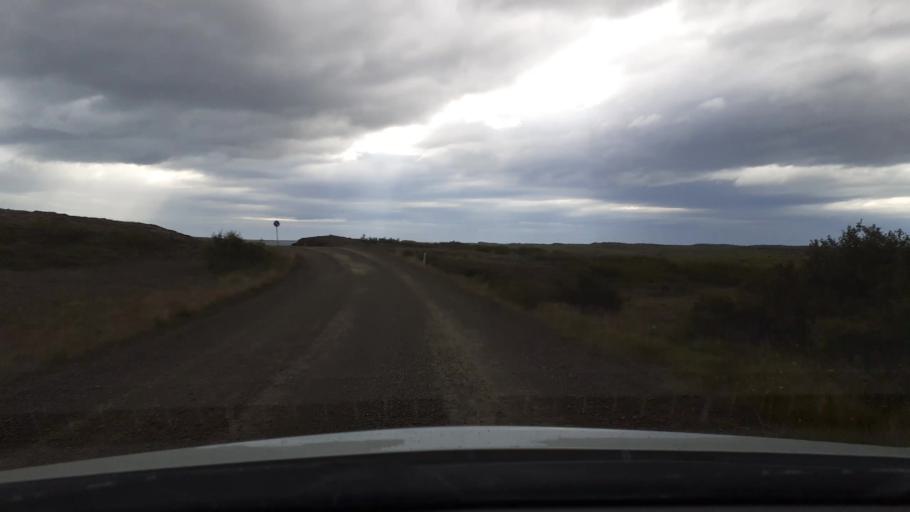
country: IS
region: West
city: Borgarnes
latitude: 64.5942
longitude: -21.9860
